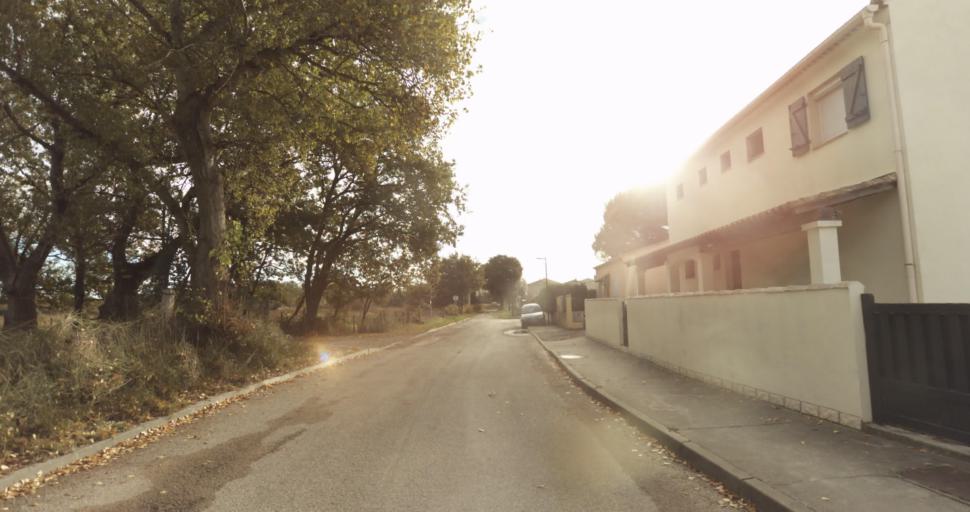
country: FR
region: Languedoc-Roussillon
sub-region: Departement du Gard
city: Aigues-Mortes
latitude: 43.5700
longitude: 4.2030
